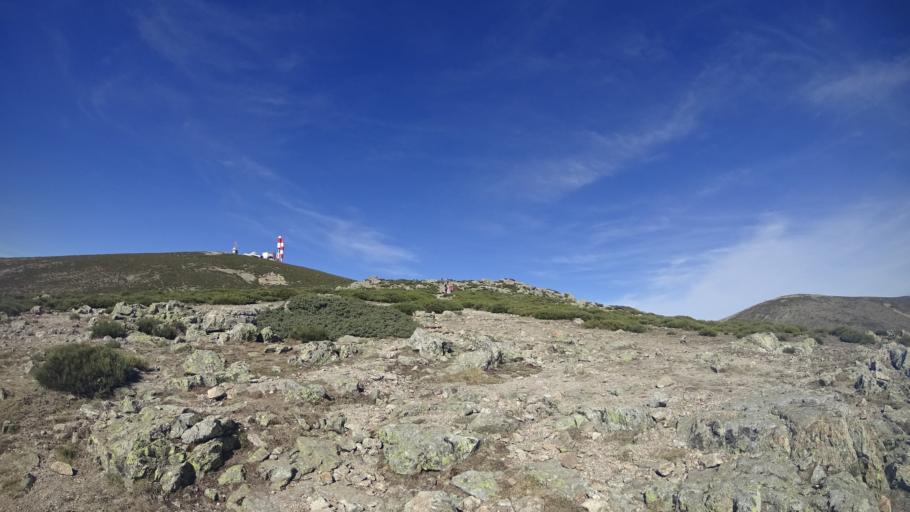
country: ES
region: Madrid
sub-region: Provincia de Madrid
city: Becerril de la Sierra
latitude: 40.7797
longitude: -3.9743
